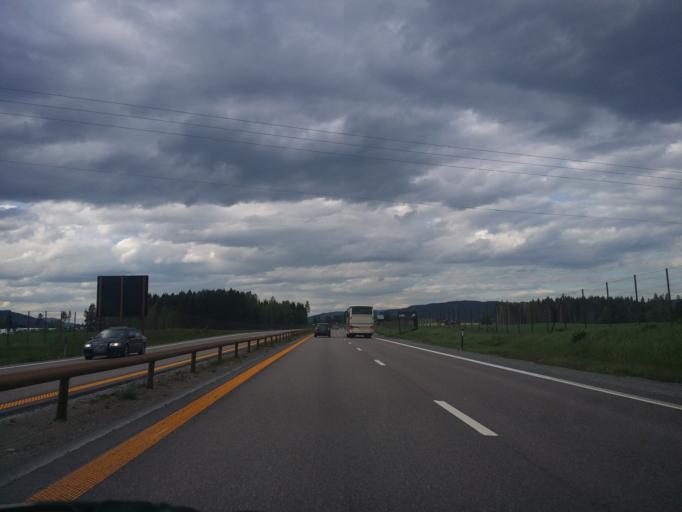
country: NO
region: Akershus
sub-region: Eidsvoll
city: Eidsvoll
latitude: 60.3830
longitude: 11.2109
